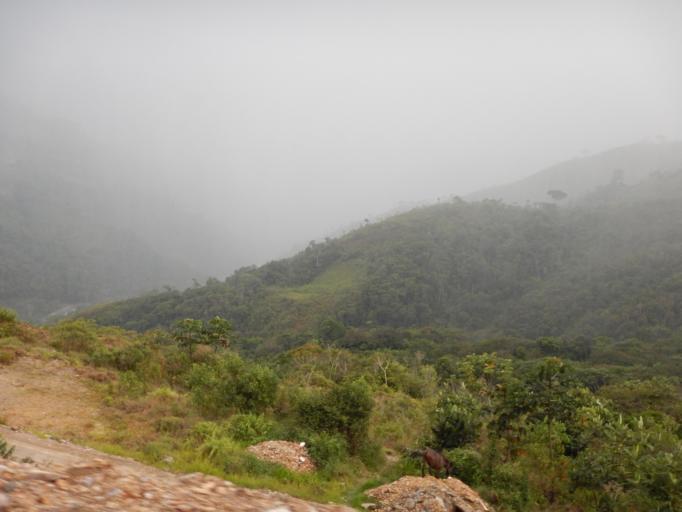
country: BO
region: La Paz
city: Coroico
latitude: -16.1101
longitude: -67.7759
